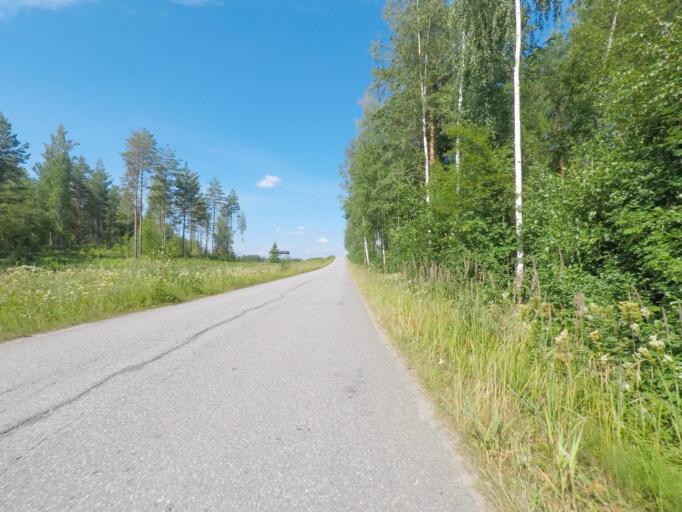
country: FI
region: Southern Savonia
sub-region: Mikkeli
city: Puumala
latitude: 61.4121
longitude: 28.0924
